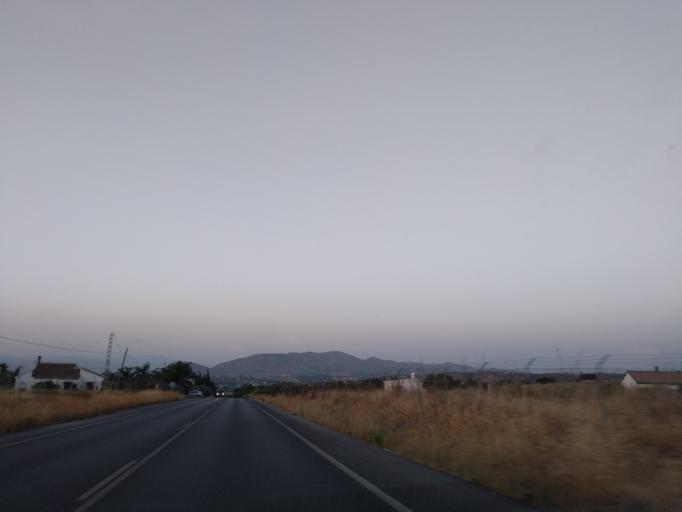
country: ES
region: Andalusia
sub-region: Provincia de Malaga
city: Alhaurin el Grande
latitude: 36.6582
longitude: -4.6740
